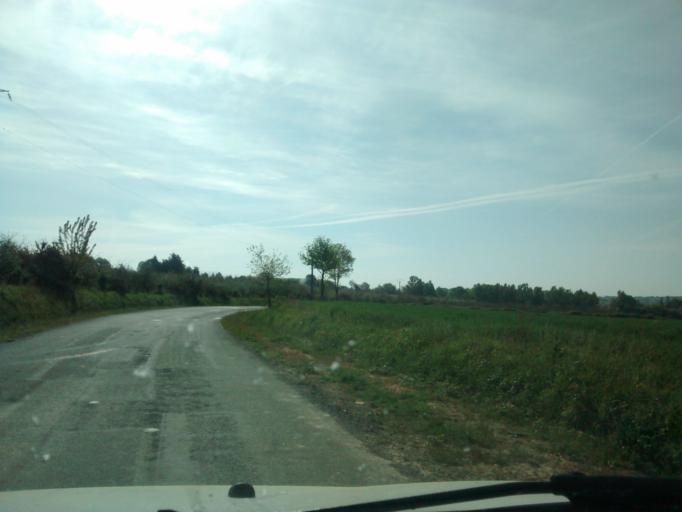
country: FR
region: Brittany
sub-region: Departement d'Ille-et-Vilaine
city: Bain-de-Bretagne
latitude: 47.8246
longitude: -1.6935
